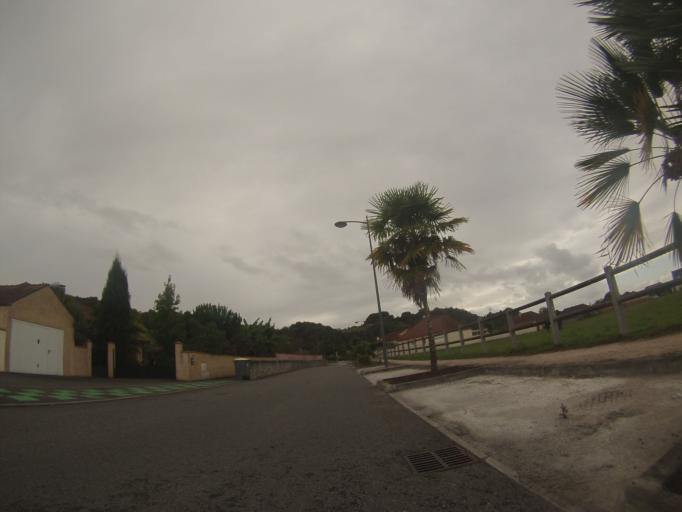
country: FR
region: Aquitaine
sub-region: Departement des Pyrenees-Atlantiques
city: Bizanos
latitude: 43.2757
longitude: -0.3539
